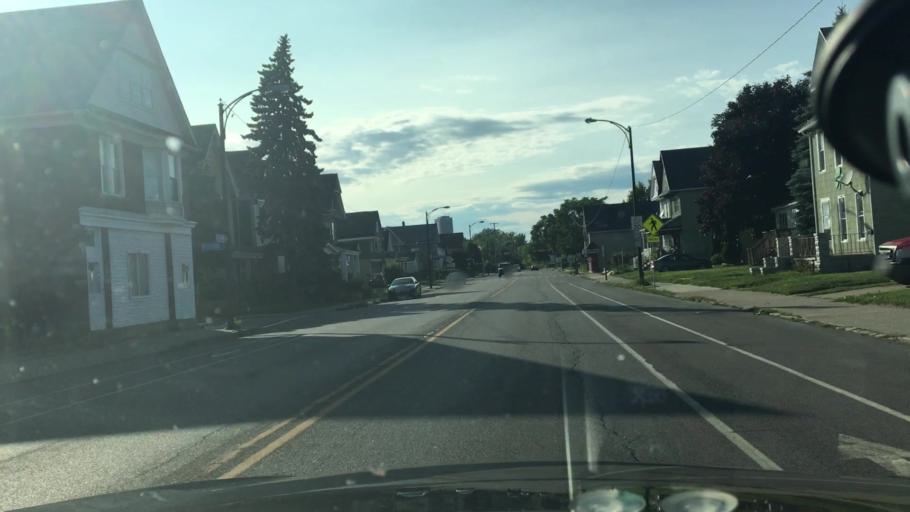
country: US
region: New York
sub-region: Erie County
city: Buffalo
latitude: 42.8664
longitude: -78.8482
